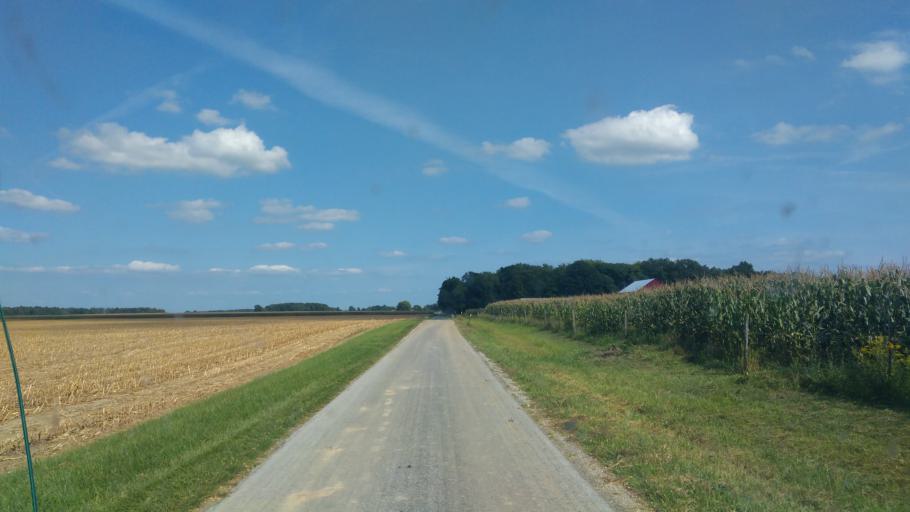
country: US
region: Ohio
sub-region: Hardin County
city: Kenton
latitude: 40.6284
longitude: -83.4878
